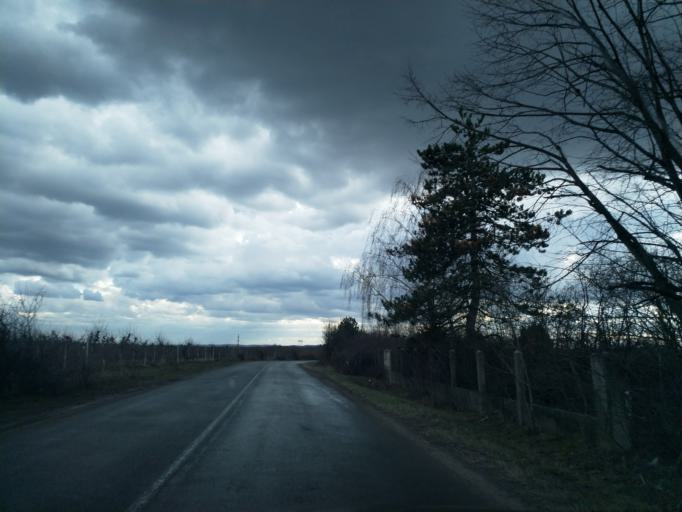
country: RS
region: Central Serbia
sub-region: Belgrade
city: Grocka
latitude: 44.6365
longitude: 20.7501
